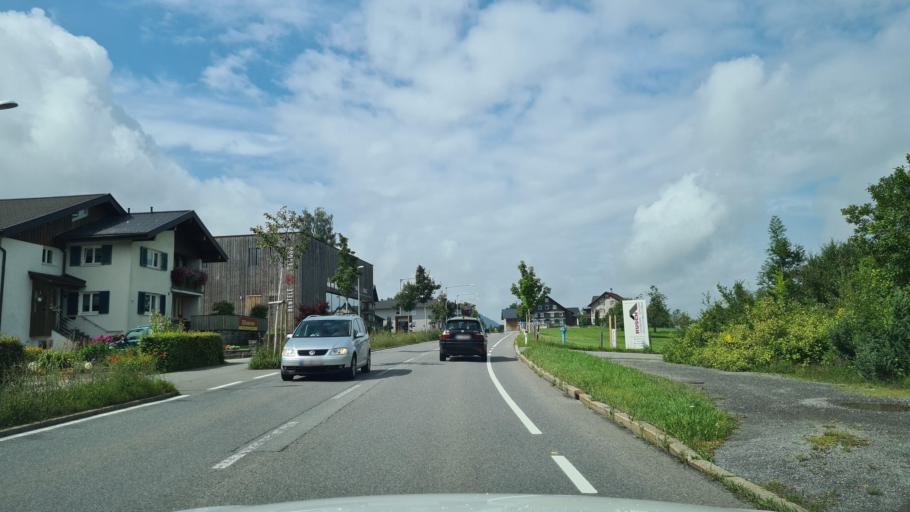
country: AT
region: Vorarlberg
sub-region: Politischer Bezirk Bregenz
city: Doren
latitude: 47.4551
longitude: 9.8437
